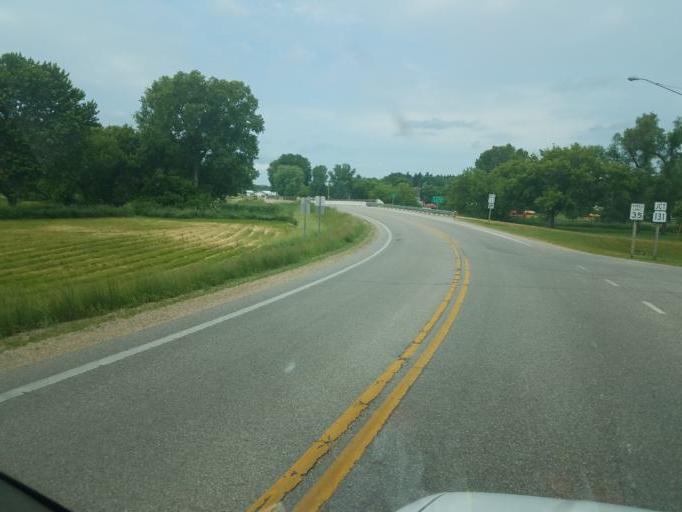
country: US
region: Wisconsin
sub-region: Monroe County
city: Cashton
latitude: 43.7214
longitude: -90.5865
